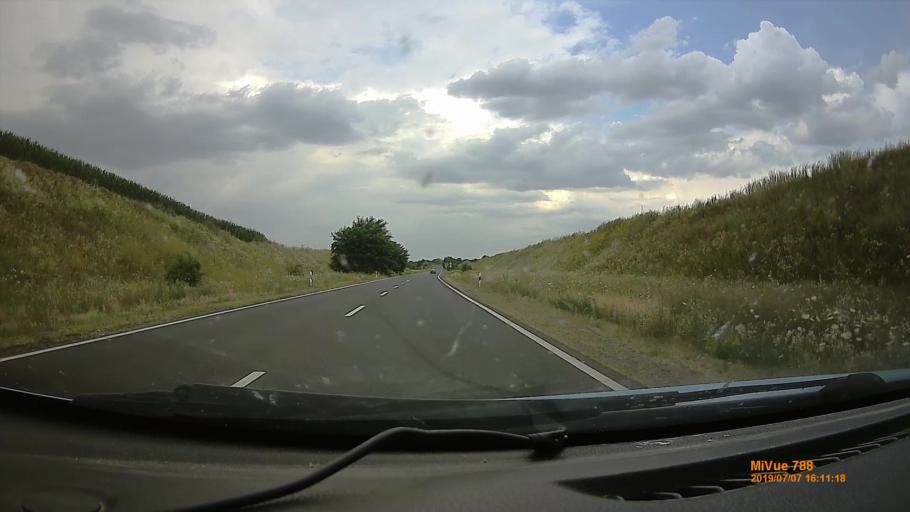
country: HU
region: Heves
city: Hatvan
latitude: 47.6750
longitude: 19.7167
